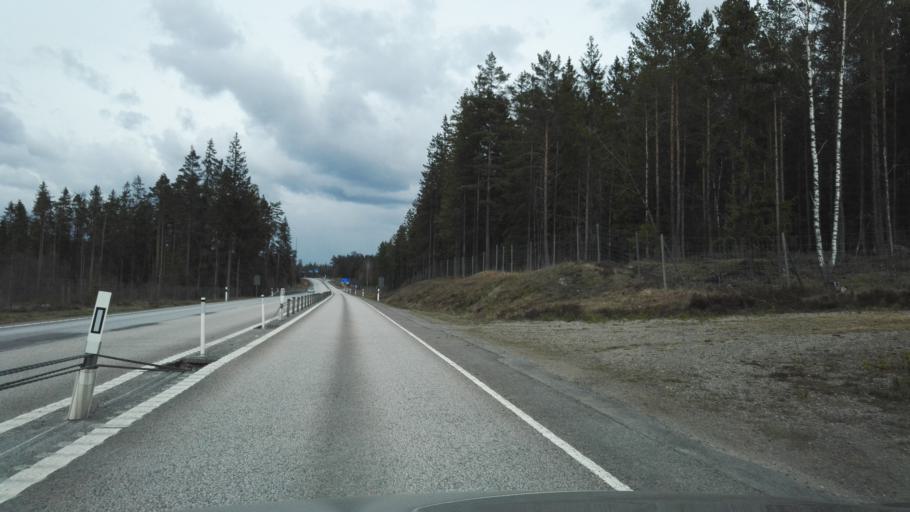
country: SE
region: Kronoberg
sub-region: Vaxjo Kommun
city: Braas
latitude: 57.0103
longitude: 15.0471
